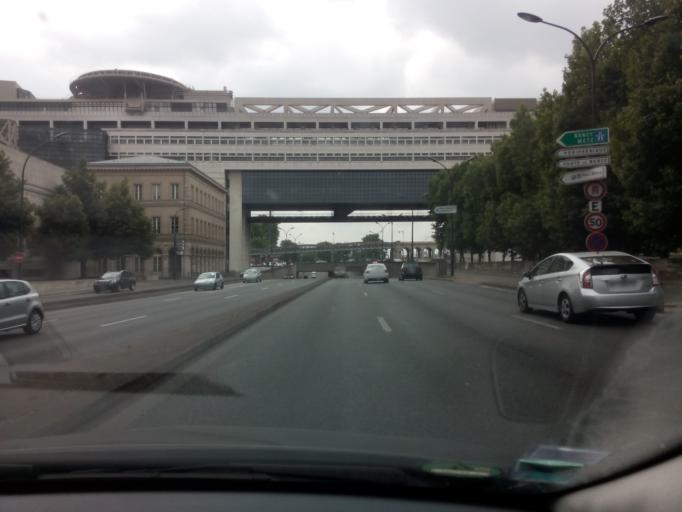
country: FR
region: Ile-de-France
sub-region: Departement du Val-de-Marne
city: Ivry-sur-Seine
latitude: 48.8402
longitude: 2.3743
